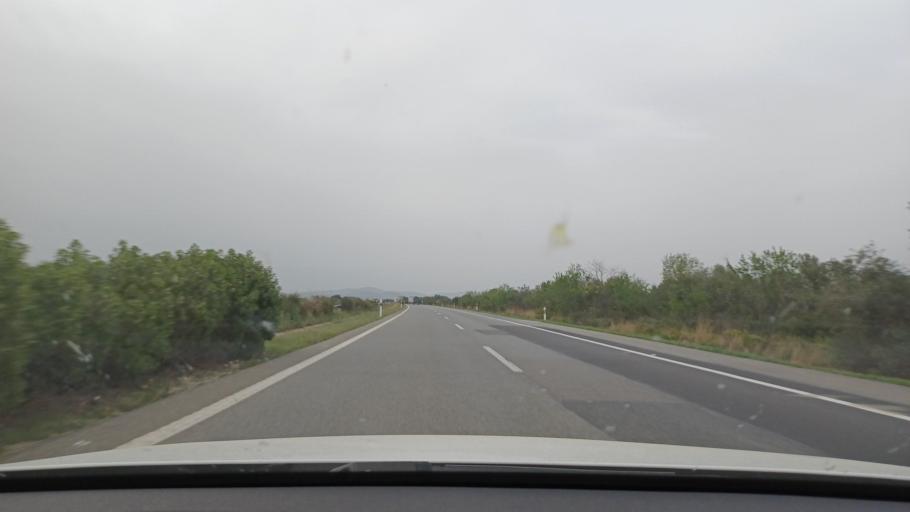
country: ES
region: Catalonia
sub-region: Provincia de Tarragona
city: Alcanar
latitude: 40.5259
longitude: 0.4174
